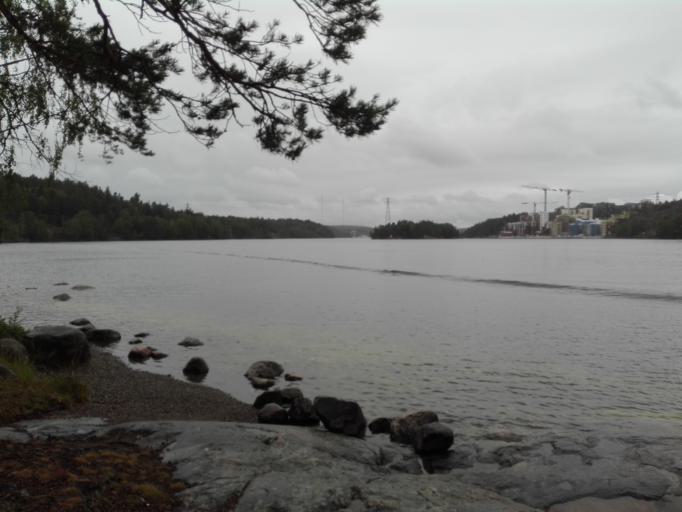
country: SE
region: Stockholm
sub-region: Nacka Kommun
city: Fisksatra
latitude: 59.2979
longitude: 18.2525
